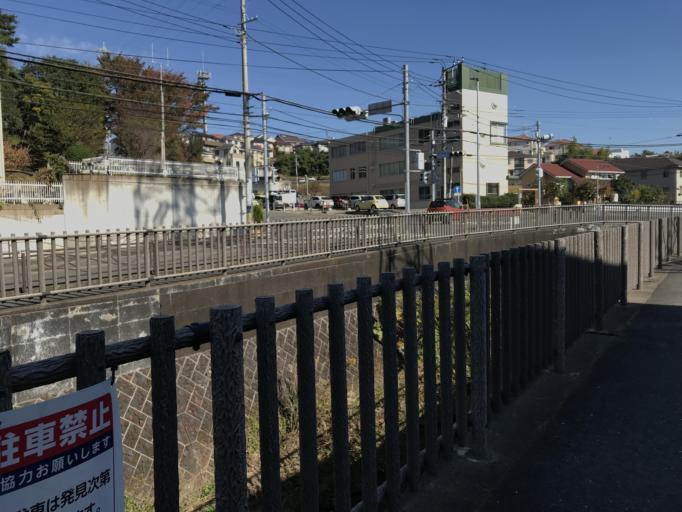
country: JP
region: Tokyo
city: Chofugaoka
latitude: 35.6024
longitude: 139.5492
